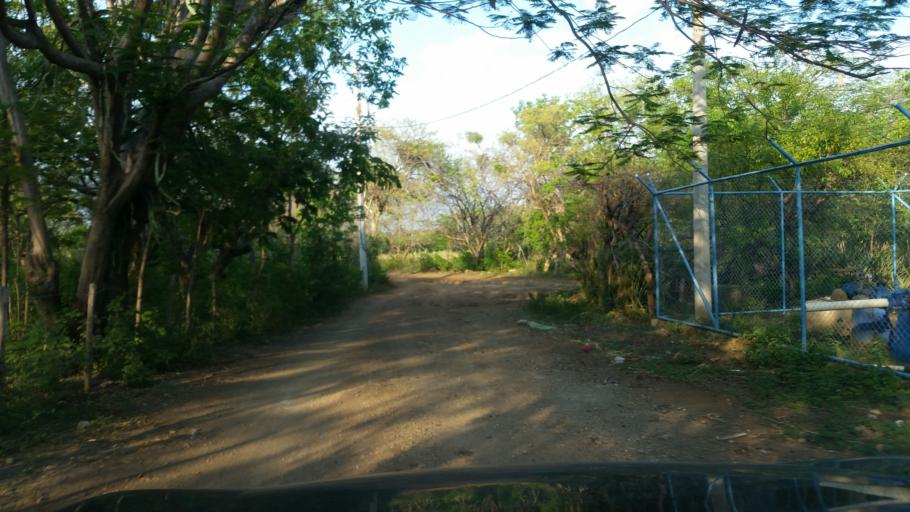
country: NI
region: Managua
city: Masachapa
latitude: 11.7770
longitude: -86.4786
